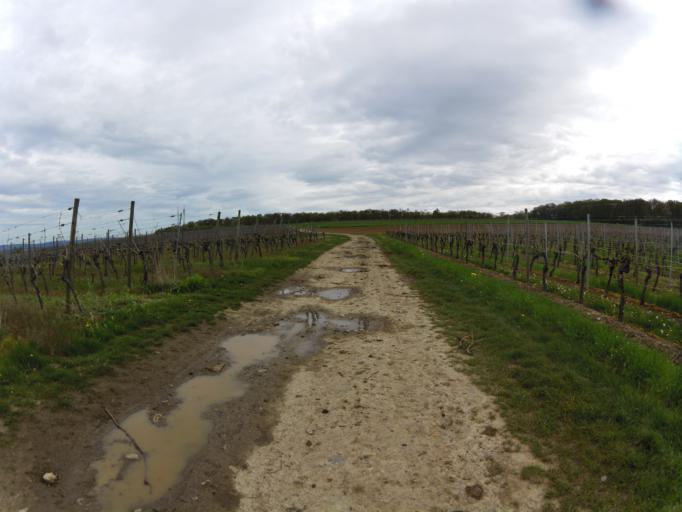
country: DE
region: Bavaria
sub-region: Regierungsbezirk Unterfranken
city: Prosselsheim
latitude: 49.8617
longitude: 10.1584
